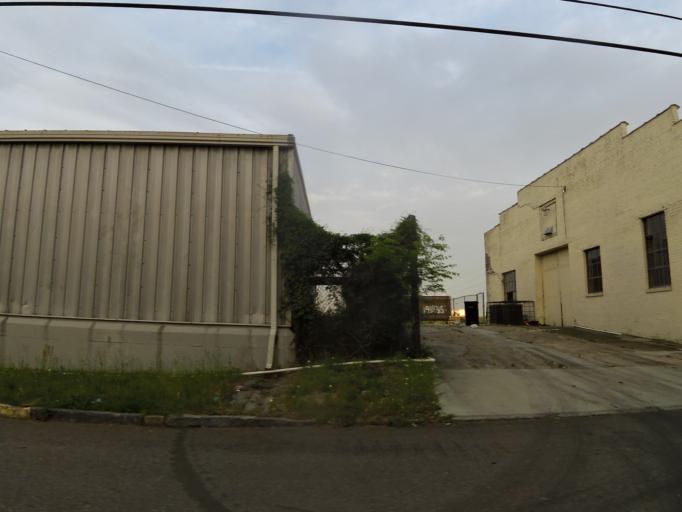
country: US
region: Georgia
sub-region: Chatham County
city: Savannah
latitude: 32.0762
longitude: -81.0826
